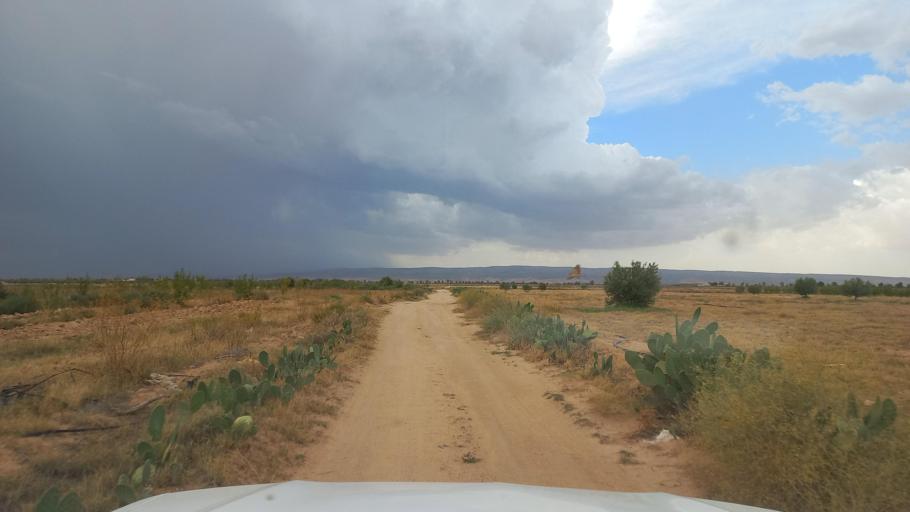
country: TN
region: Al Qasrayn
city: Kasserine
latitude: 35.2367
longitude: 9.0163
